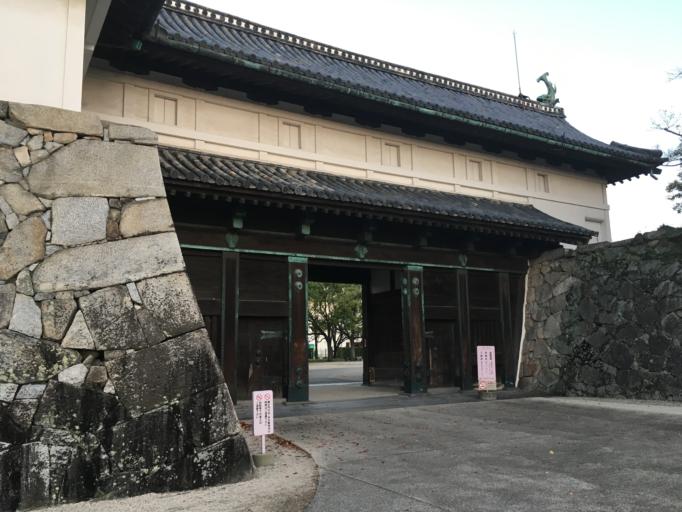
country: JP
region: Saga Prefecture
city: Saga-shi
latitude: 33.2460
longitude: 130.3027
